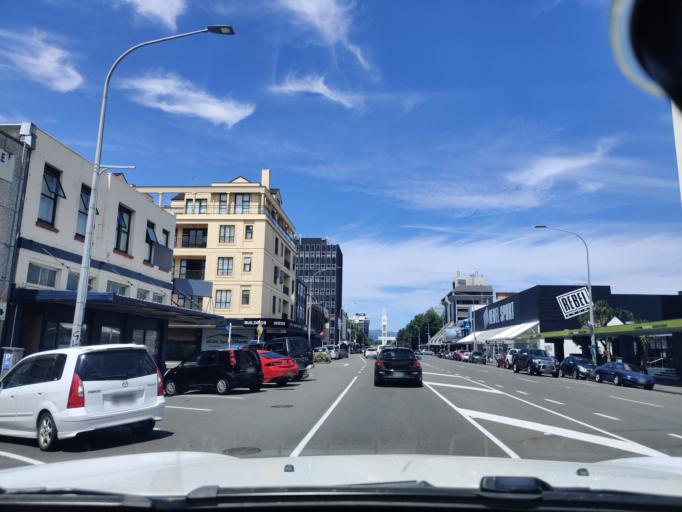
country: NZ
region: Manawatu-Wanganui
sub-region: Palmerston North City
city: Palmerston North
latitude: -40.3534
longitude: 175.6090
